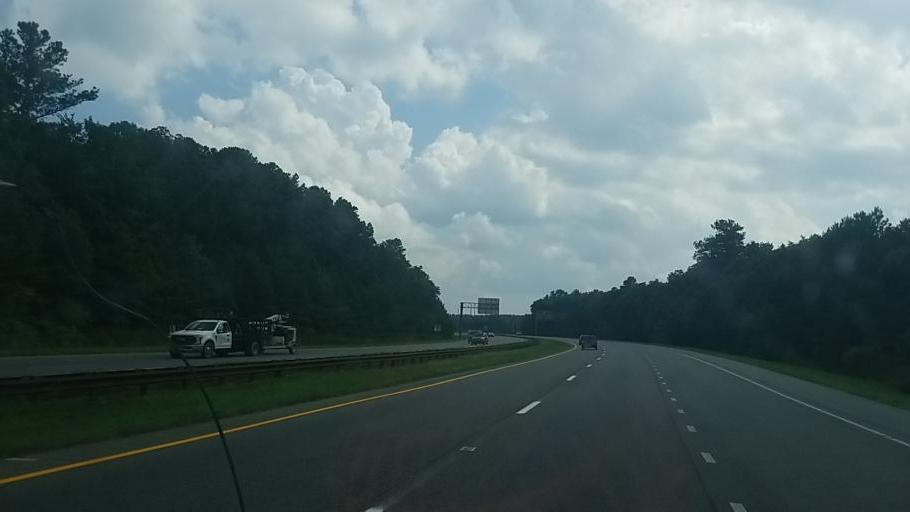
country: US
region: Maryland
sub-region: Worcester County
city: Ocean Pines
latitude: 38.3843
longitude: -75.2056
